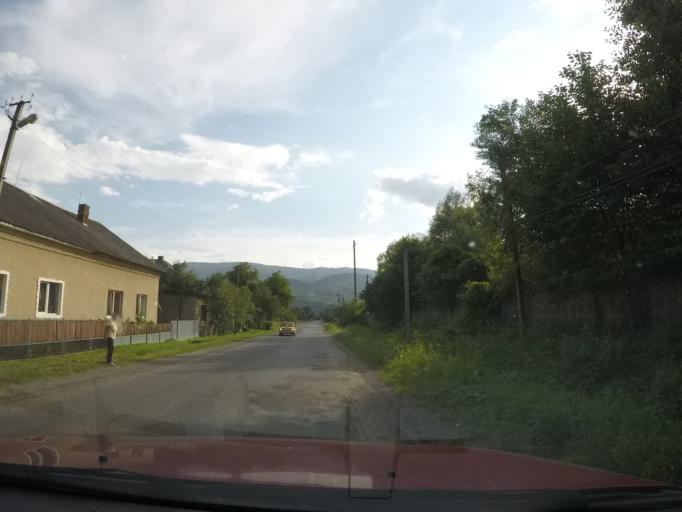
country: UA
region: Zakarpattia
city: Velykyi Bereznyi
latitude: 48.9467
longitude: 22.6012
